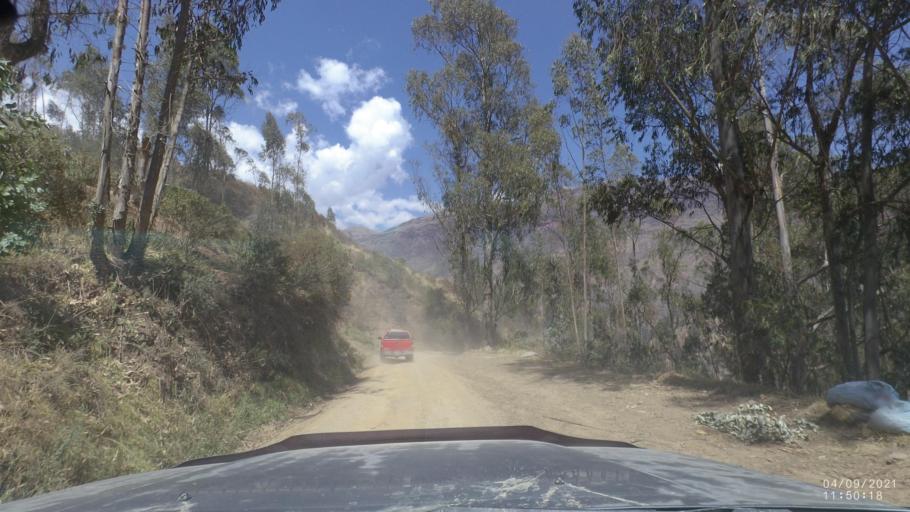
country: BO
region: Cochabamba
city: Colchani
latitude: -17.2261
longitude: -66.5253
